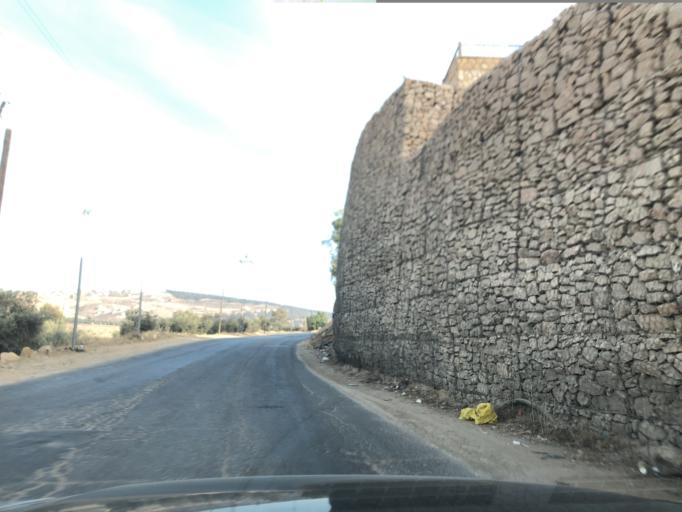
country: JO
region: Jerash
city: Jarash
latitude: 32.2670
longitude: 35.8869
